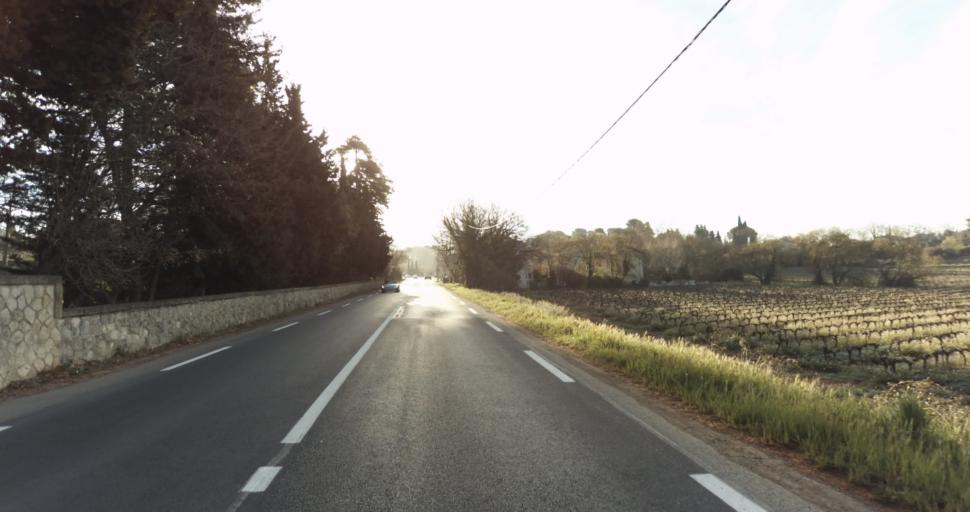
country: FR
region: Provence-Alpes-Cote d'Azur
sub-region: Departement des Bouches-du-Rhone
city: Eguilles
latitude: 43.5357
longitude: 5.3906
